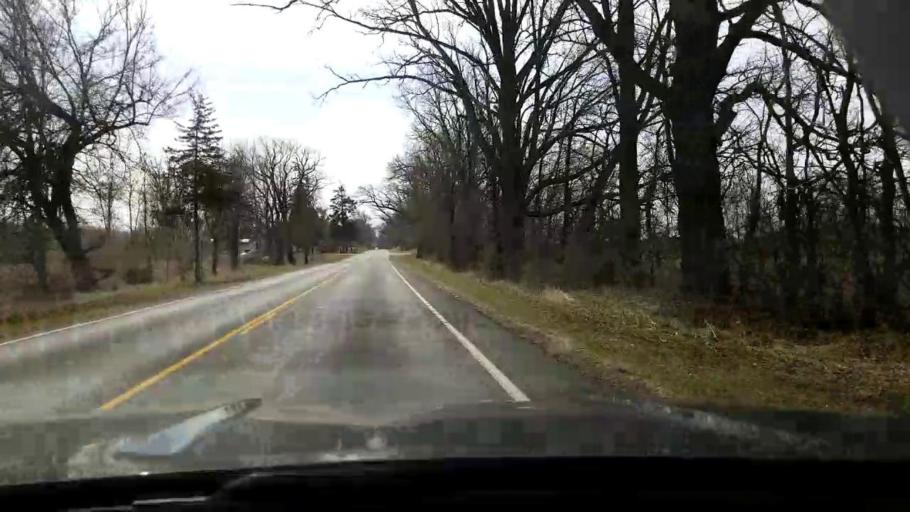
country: US
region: Michigan
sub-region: Jackson County
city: Spring Arbor
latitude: 42.1691
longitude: -84.5199
